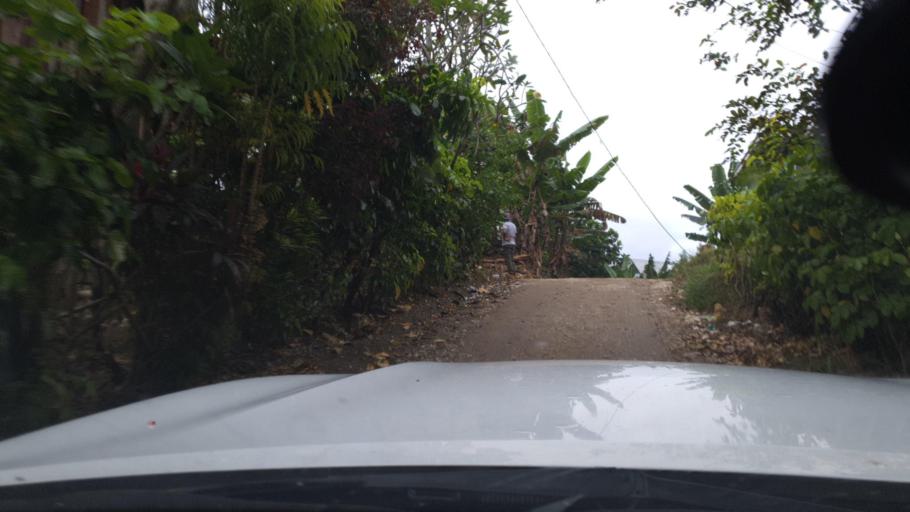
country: SB
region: Guadalcanal
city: Honiara
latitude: -9.4500
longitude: 159.9805
